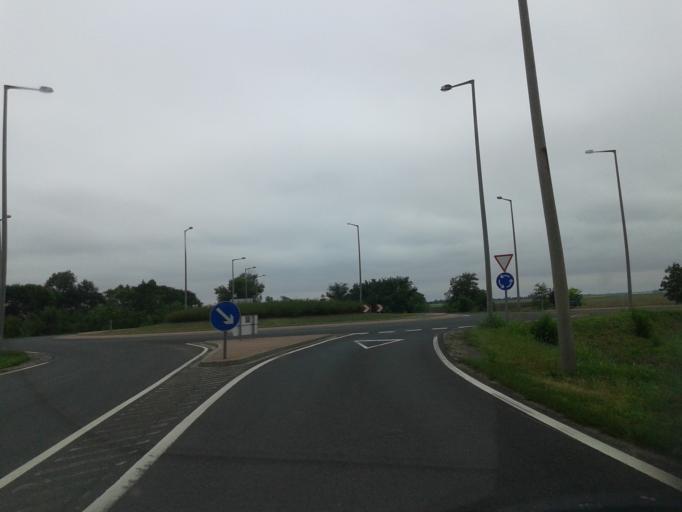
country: HU
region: Bacs-Kiskun
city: Apostag
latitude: 46.8689
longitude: 18.9794
